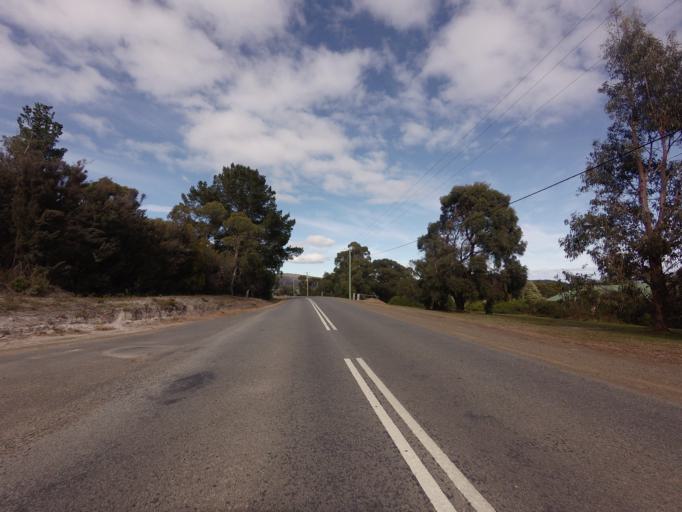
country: AU
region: Tasmania
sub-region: Clarence
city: Sandford
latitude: -43.0894
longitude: 147.7383
